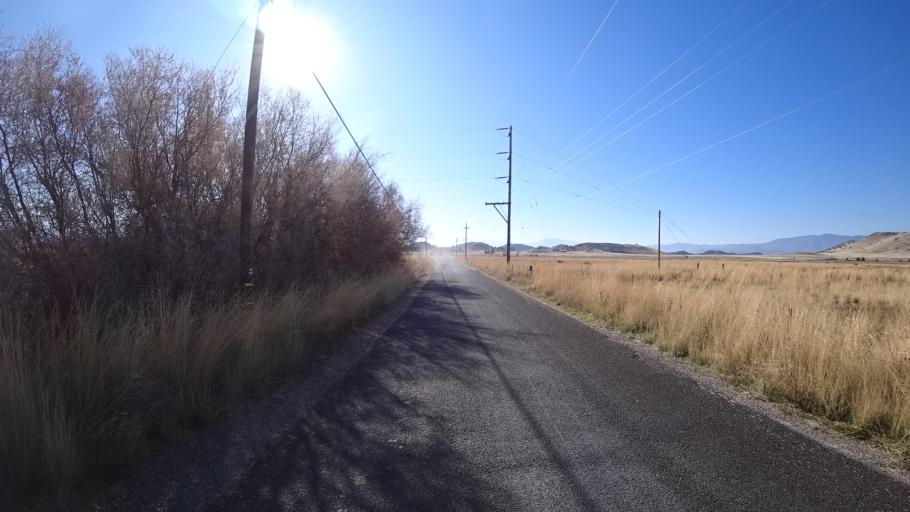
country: US
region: California
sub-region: Siskiyou County
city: Montague
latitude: 41.7117
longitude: -122.4377
